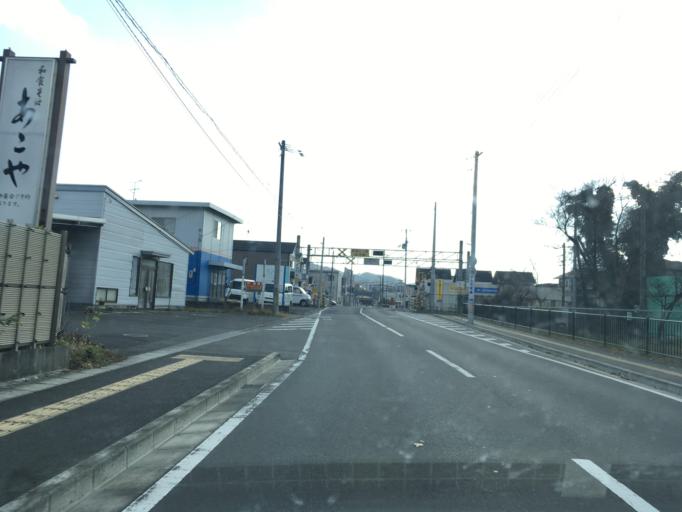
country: JP
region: Miyagi
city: Sendai
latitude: 38.2733
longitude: 140.7644
